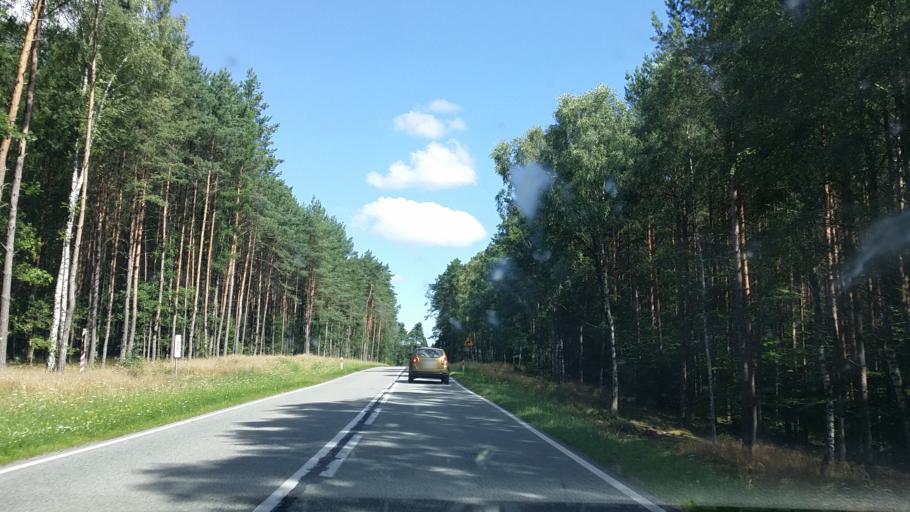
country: PL
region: West Pomeranian Voivodeship
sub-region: Powiat drawski
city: Drawsko Pomorskie
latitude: 53.4165
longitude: 15.8289
